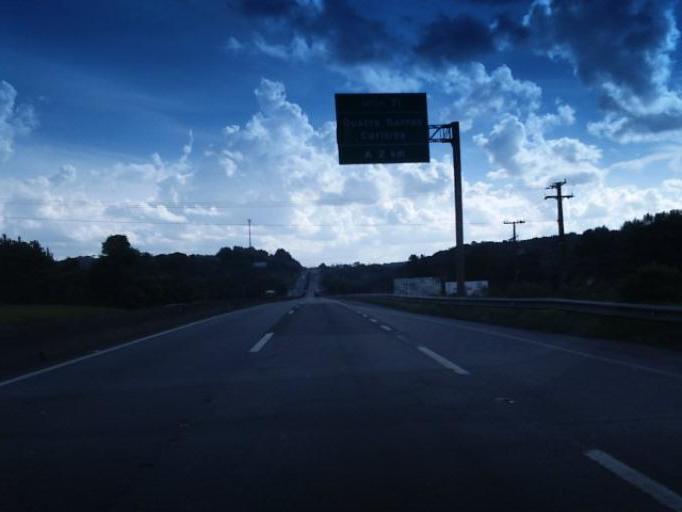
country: BR
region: Parana
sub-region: Campina Grande Do Sul
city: Campina Grande do Sul
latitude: -25.3299
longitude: -49.0305
